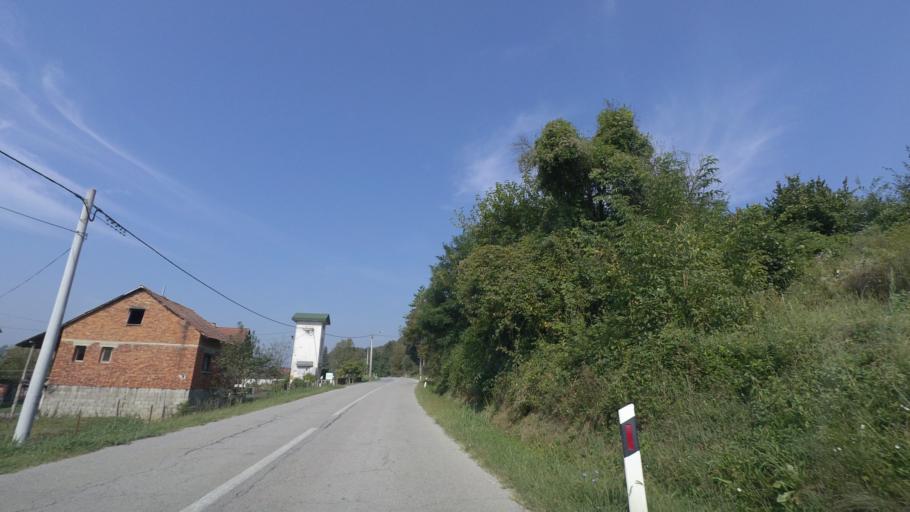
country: BA
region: Republika Srpska
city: Knezica
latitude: 45.2121
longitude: 16.6582
